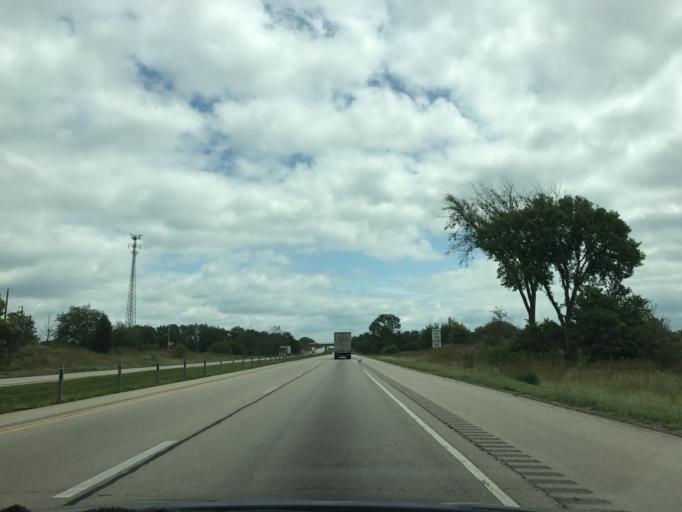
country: US
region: Illinois
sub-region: LaSalle County
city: Marseilles
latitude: 41.3753
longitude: -88.6952
